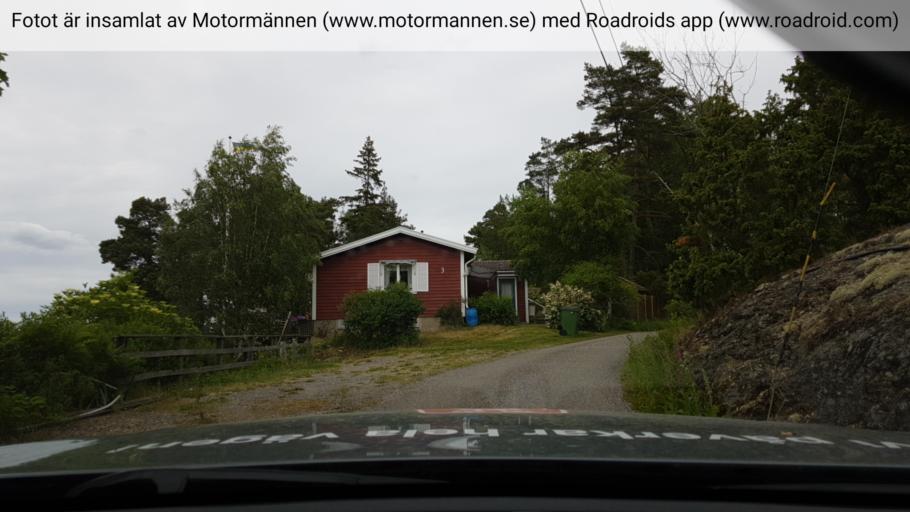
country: SE
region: Stockholm
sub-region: Haninge Kommun
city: Jordbro
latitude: 59.0191
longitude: 18.0945
